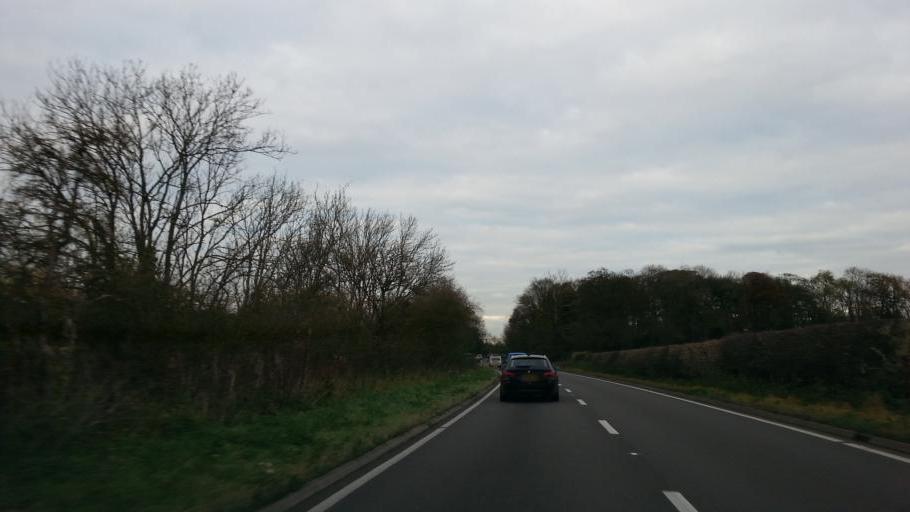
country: GB
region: England
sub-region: District of Rutland
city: South Luffenham
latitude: 52.5500
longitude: -0.5814
